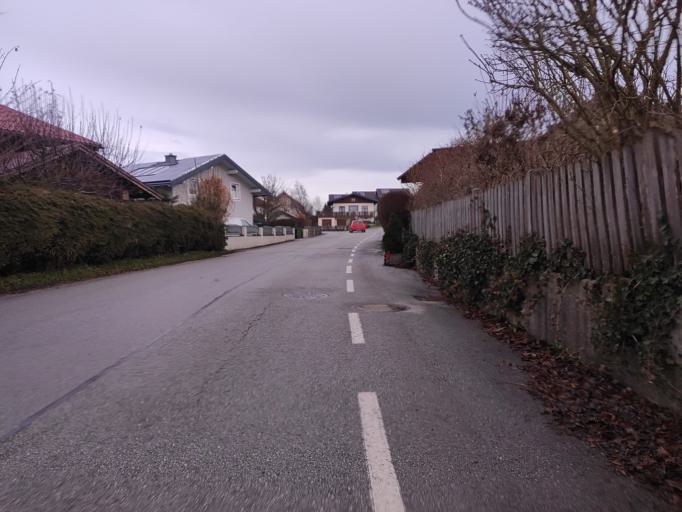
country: AT
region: Salzburg
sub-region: Politischer Bezirk Salzburg-Umgebung
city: Elixhausen
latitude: 47.8938
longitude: 13.0579
